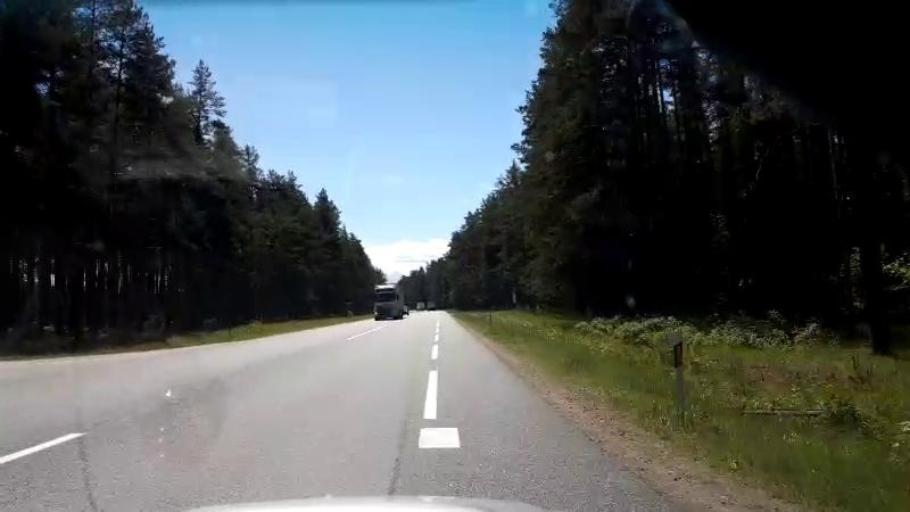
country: LV
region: Saulkrastu
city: Saulkrasti
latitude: 57.3498
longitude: 24.4389
